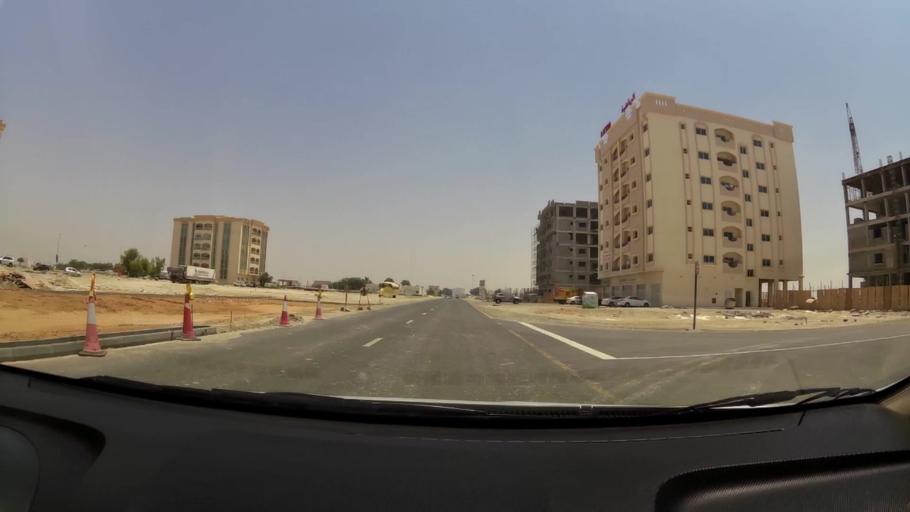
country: AE
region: Umm al Qaywayn
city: Umm al Qaywayn
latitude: 25.5160
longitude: 55.5428
